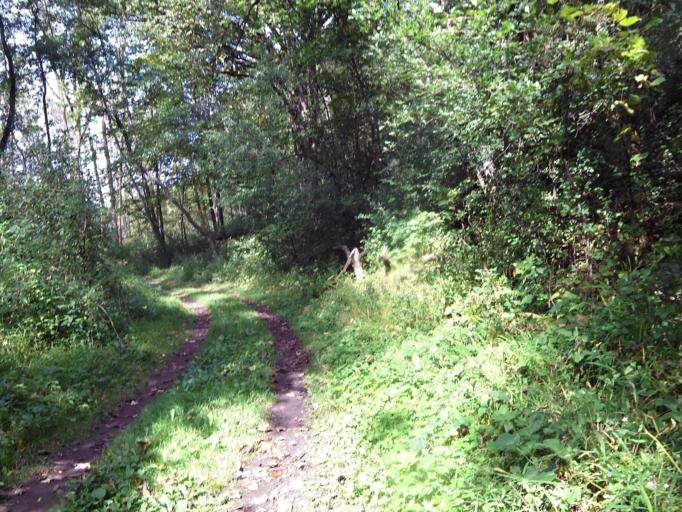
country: US
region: Minnesota
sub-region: Washington County
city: Afton
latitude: 44.8602
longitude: -92.7931
